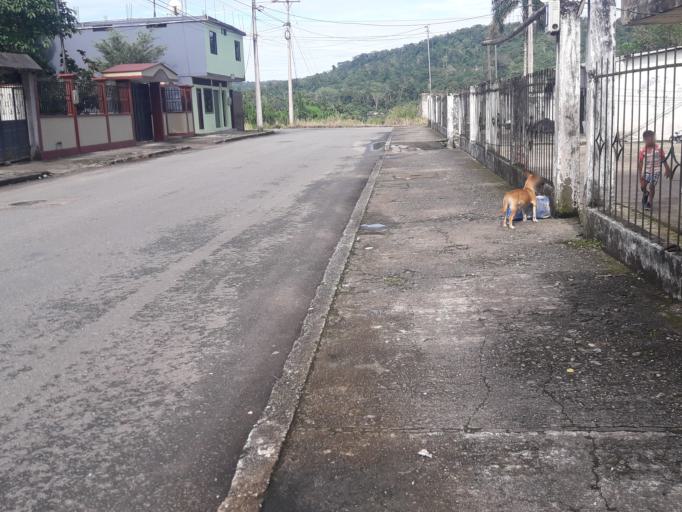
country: EC
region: Napo
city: Tena
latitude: -0.9874
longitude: -77.8121
